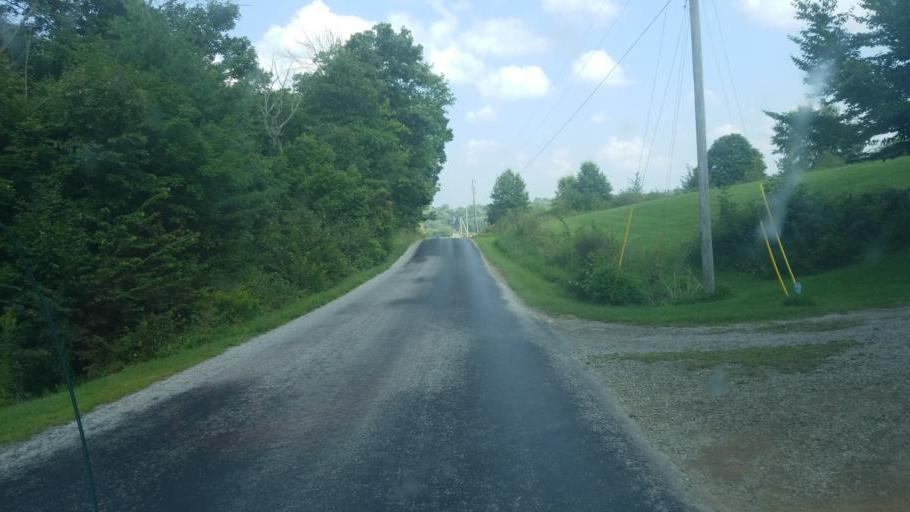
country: US
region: Ohio
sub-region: Medina County
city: Lodi
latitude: 40.9743
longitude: -82.0398
